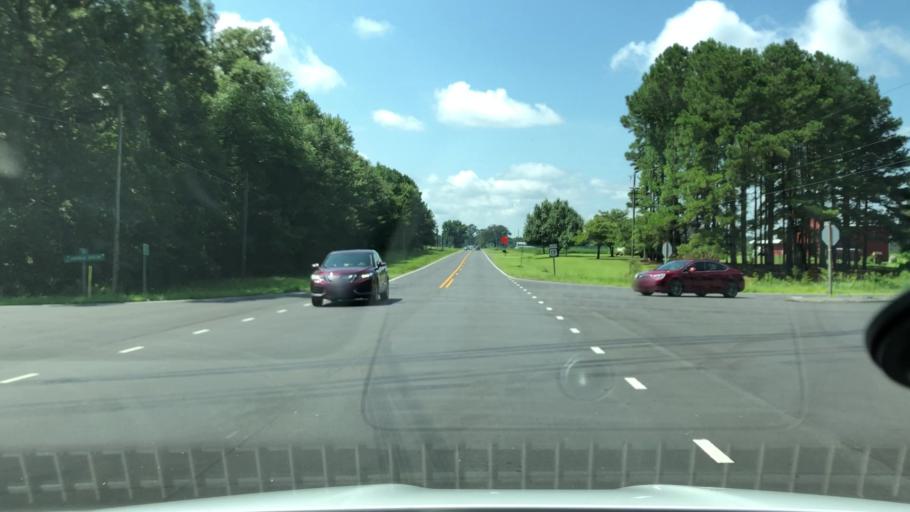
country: US
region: North Carolina
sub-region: Martin County
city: Williamston
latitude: 35.7703
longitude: -77.0698
